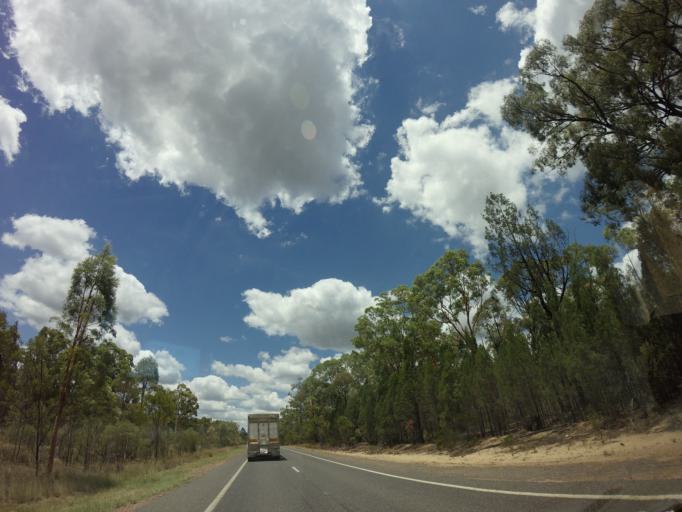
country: AU
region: Queensland
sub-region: Goondiwindi
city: Goondiwindi
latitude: -27.9934
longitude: 150.9538
